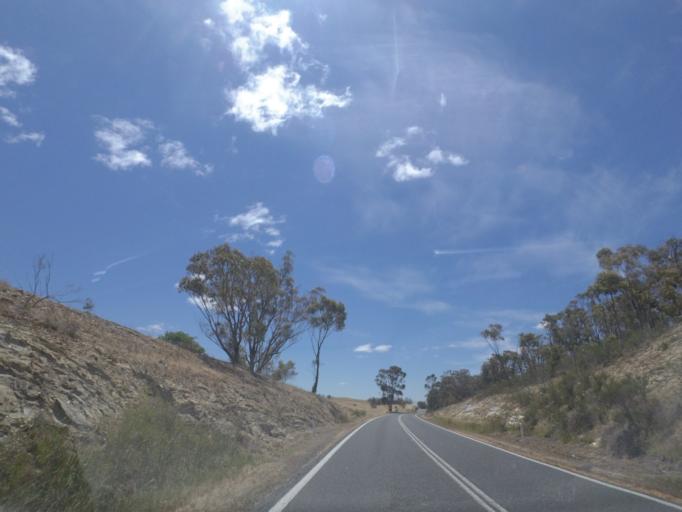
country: AU
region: Victoria
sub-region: Mount Alexander
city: Castlemaine
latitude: -37.2141
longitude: 144.1401
